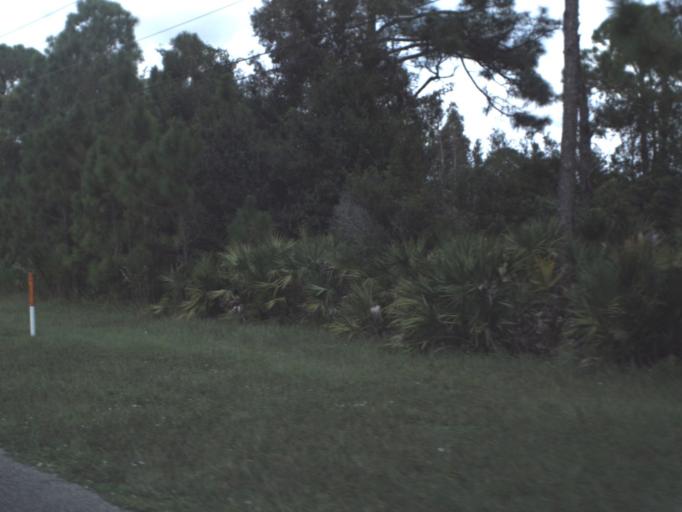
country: US
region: Florida
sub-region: Charlotte County
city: Charlotte Park
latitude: 26.8642
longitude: -81.9946
